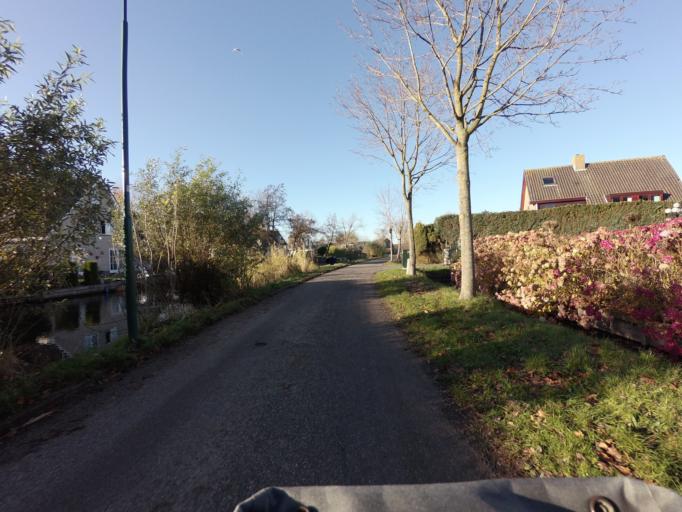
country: NL
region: Utrecht
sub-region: Stichtse Vecht
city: Vreeland
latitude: 52.2473
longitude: 4.9887
